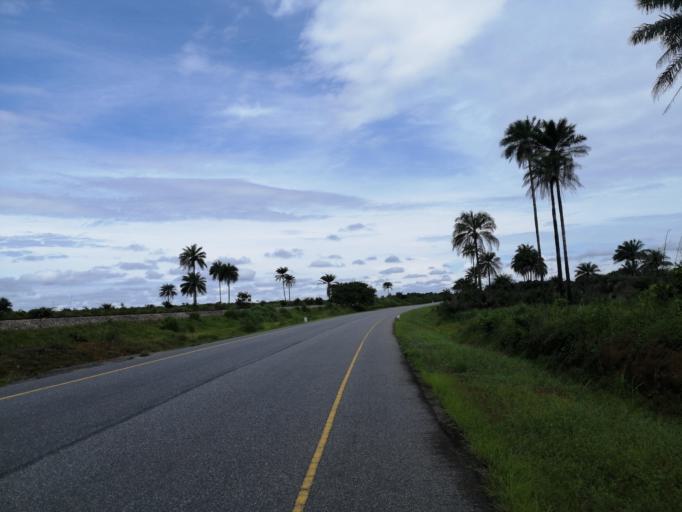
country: SL
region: Northern Province
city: Port Loko
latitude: 8.7465
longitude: -12.9223
